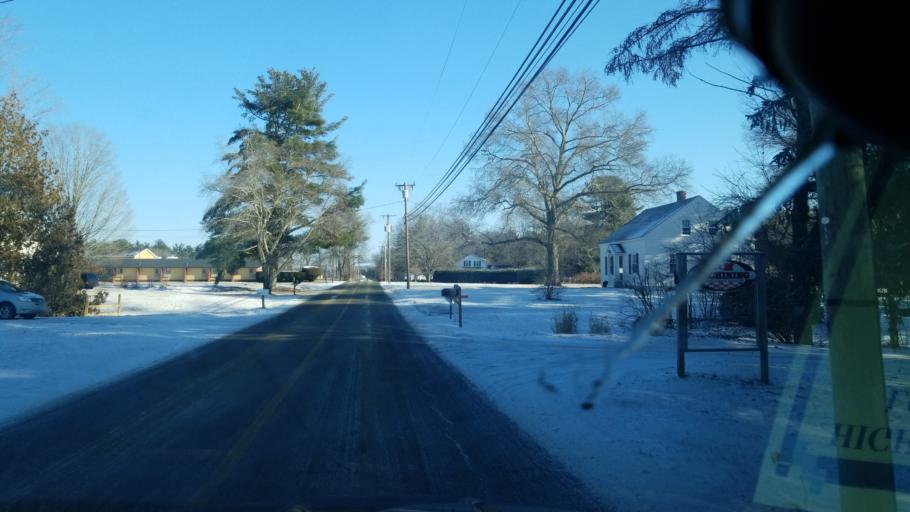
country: US
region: Connecticut
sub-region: Windham County
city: East Brooklyn
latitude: 41.7958
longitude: -71.9099
